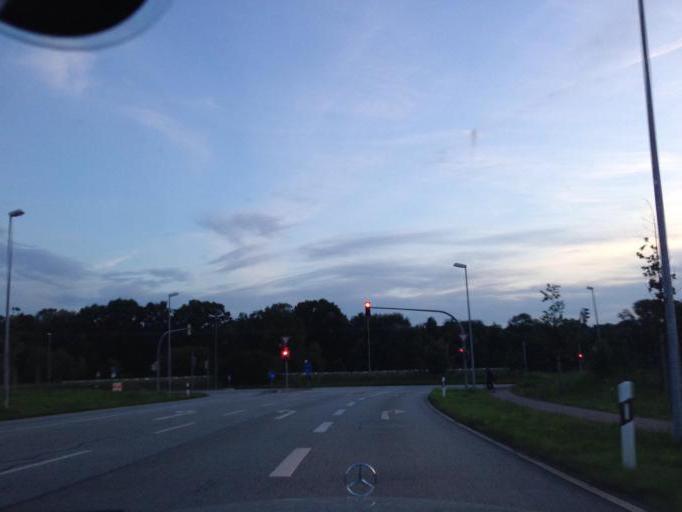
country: DE
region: Schleswig-Holstein
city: Delingsdorf
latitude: 53.6747
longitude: 10.2569
